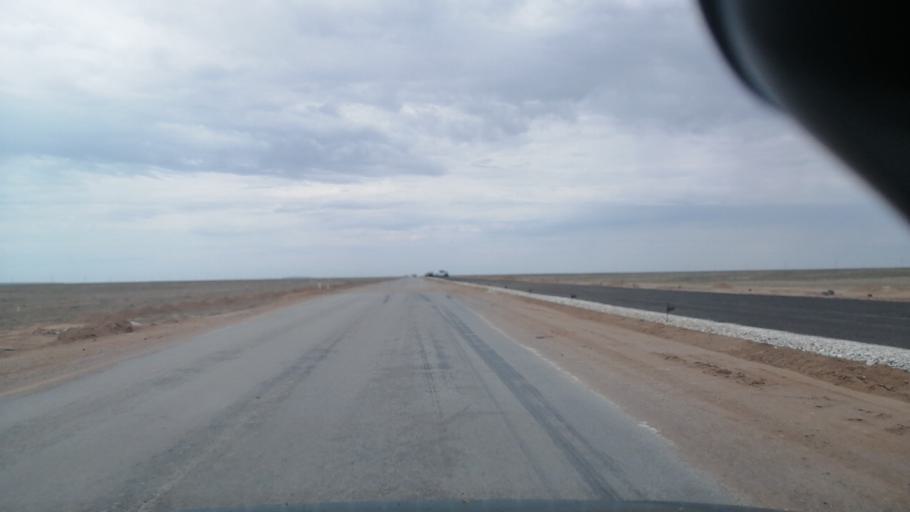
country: KZ
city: Priozersk
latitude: 46.5625
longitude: 74.2049
